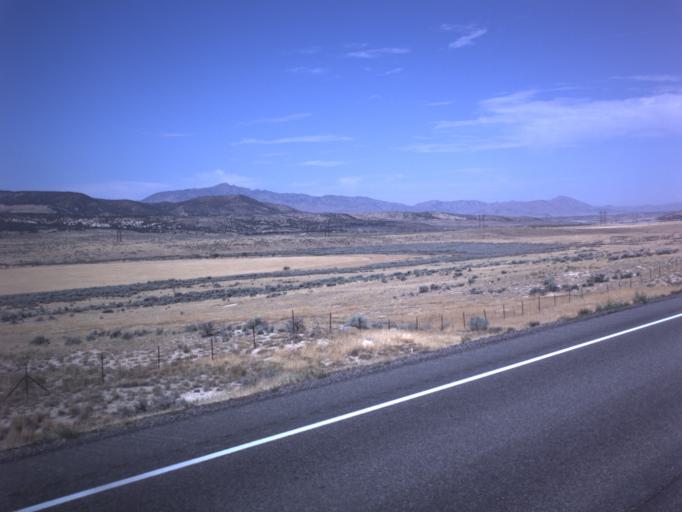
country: US
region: Utah
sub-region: Sanpete County
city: Gunnison
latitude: 39.3243
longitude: -111.9099
